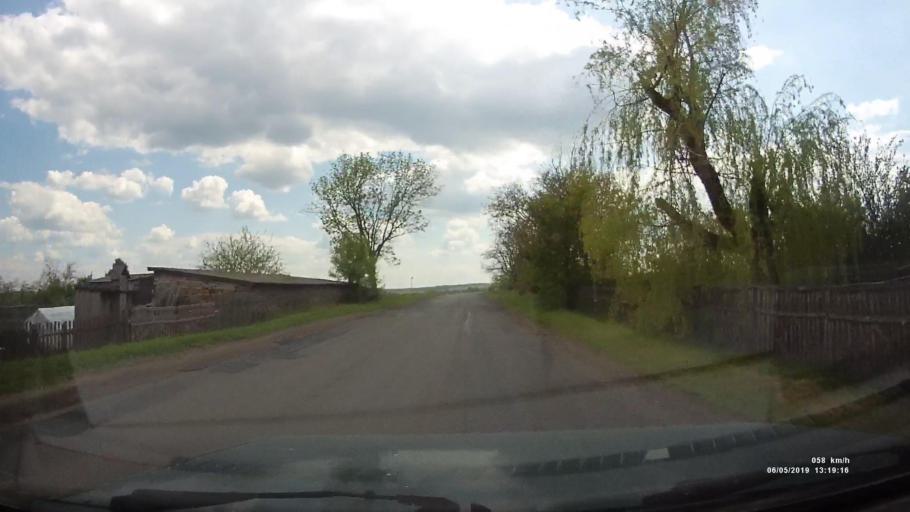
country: RU
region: Rostov
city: Ust'-Donetskiy
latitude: 47.7268
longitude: 40.9141
